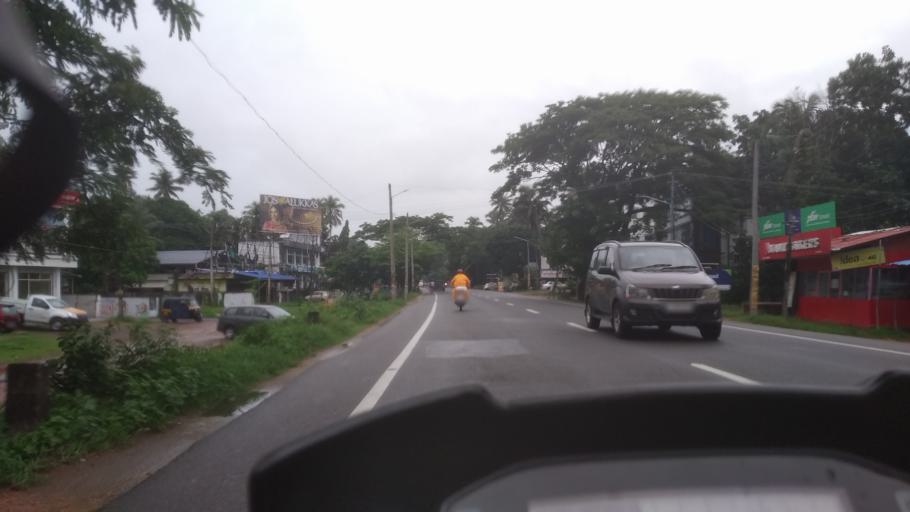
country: IN
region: Kerala
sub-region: Alappuzha
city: Kayankulam
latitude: 9.1830
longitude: 76.4908
